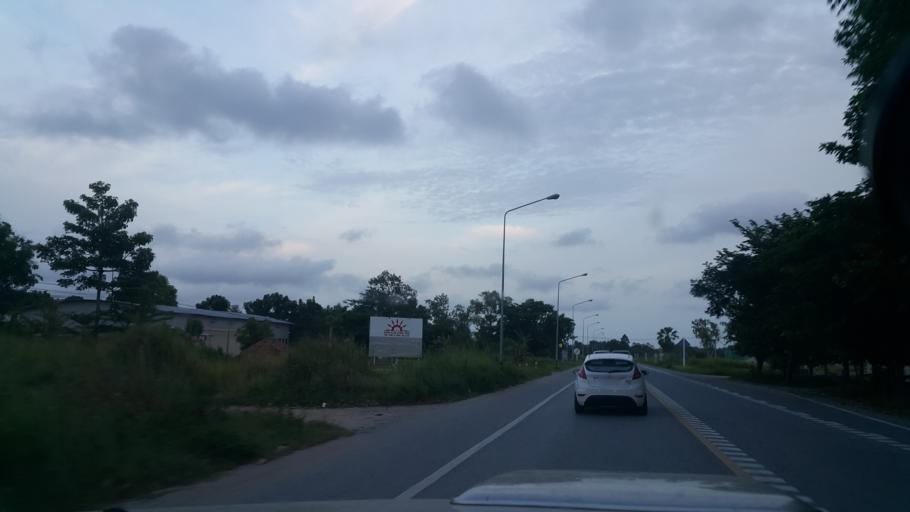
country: TH
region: Rayong
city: Ban Chang
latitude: 12.7127
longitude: 101.0029
